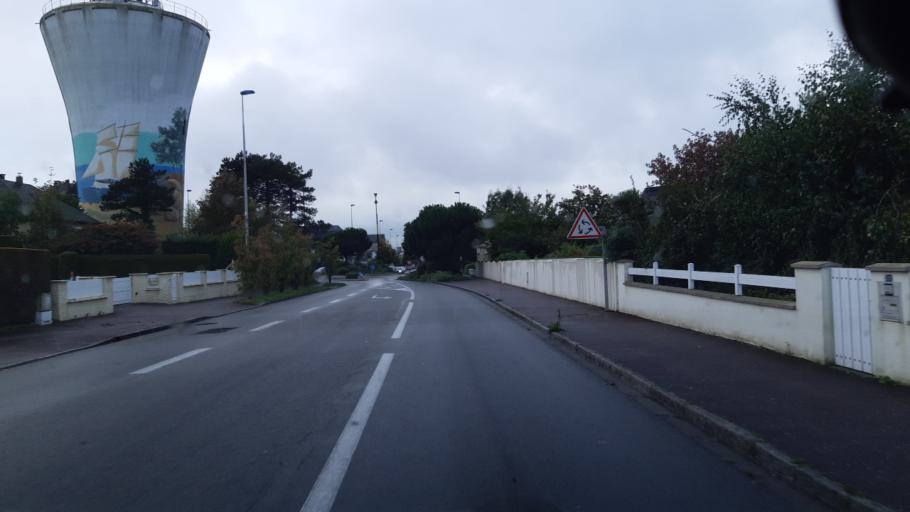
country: FR
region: Lower Normandy
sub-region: Departement de la Manche
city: Donville-les-Bains
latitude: 48.8546
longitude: -1.5640
